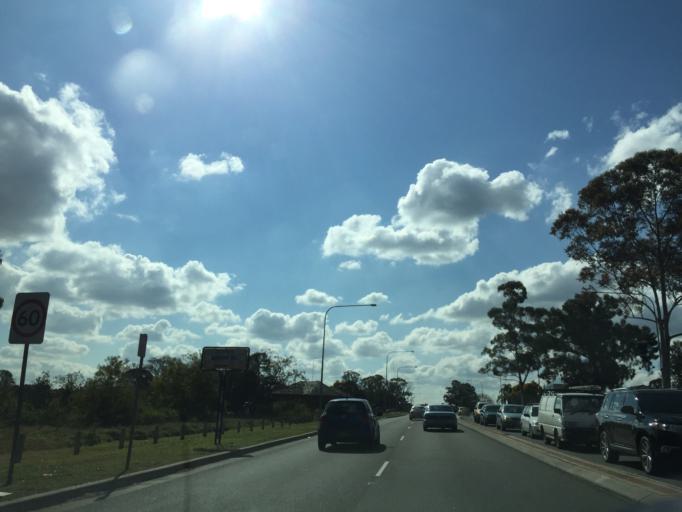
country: AU
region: New South Wales
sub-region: Blacktown
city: Quakers Hill
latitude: -33.7423
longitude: 150.8705
